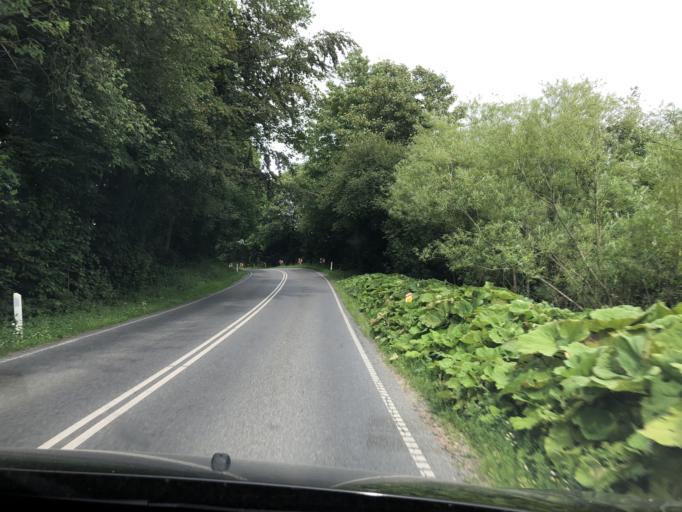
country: DK
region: South Denmark
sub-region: Assens Kommune
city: Glamsbjerg
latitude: 55.2909
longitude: 10.0849
